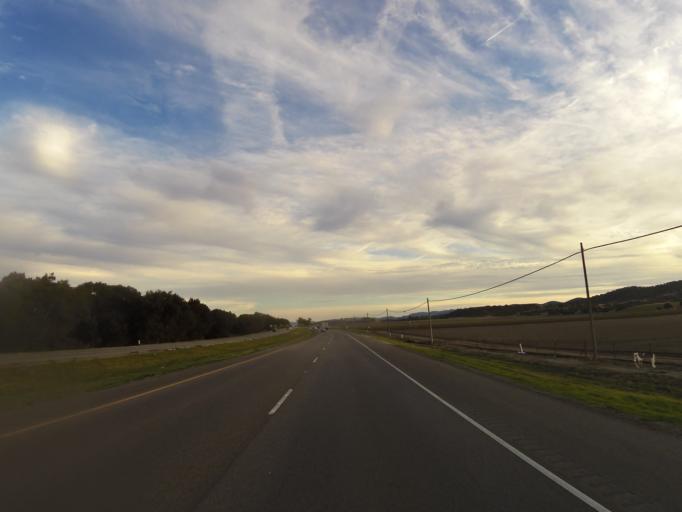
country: US
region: California
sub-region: Monterey County
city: King City
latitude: 36.2072
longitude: -121.1594
